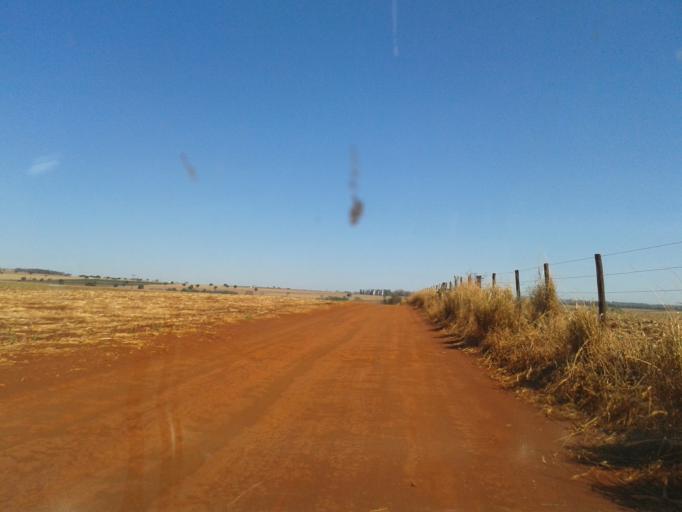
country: BR
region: Minas Gerais
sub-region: Centralina
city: Centralina
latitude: -18.5903
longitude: -49.1615
